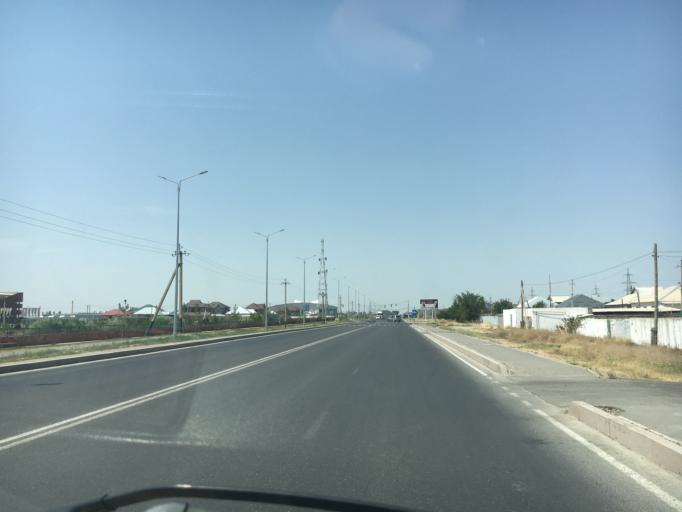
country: KZ
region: Zhambyl
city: Taraz
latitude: 42.8811
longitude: 71.3224
